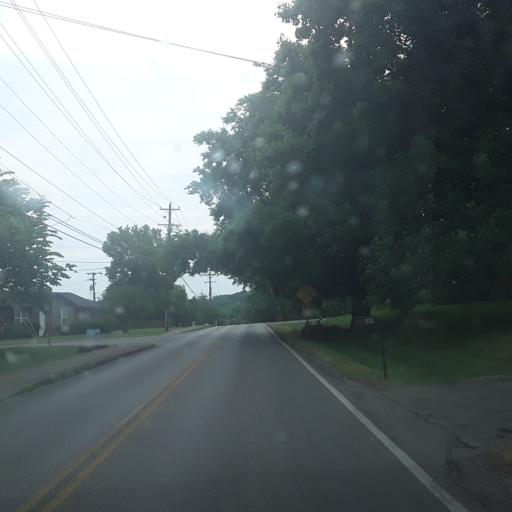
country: US
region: Tennessee
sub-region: Williamson County
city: Brentwood
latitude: 36.0550
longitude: -86.7310
